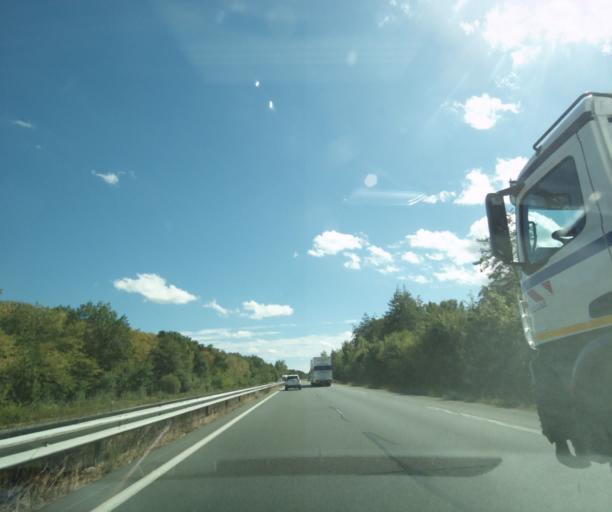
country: FR
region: Aquitaine
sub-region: Departement du Lot-et-Garonne
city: Fourques-sur-Garonne
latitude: 44.4141
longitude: 0.1783
